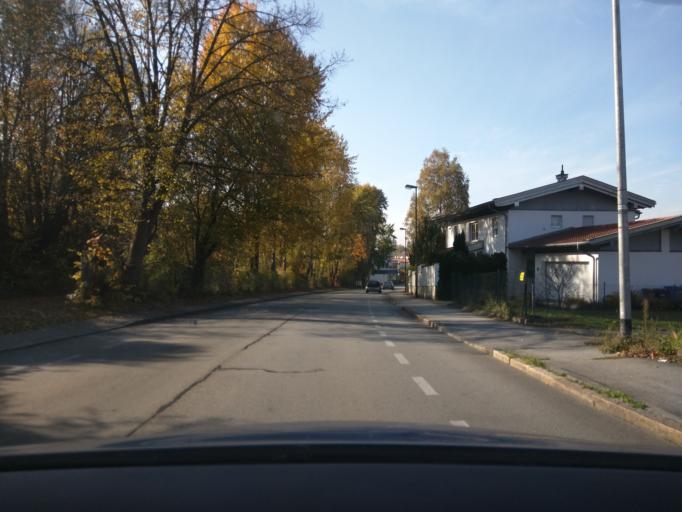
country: DE
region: Bavaria
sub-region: Lower Bavaria
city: Salzweg
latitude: 48.5708
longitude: 13.4830
